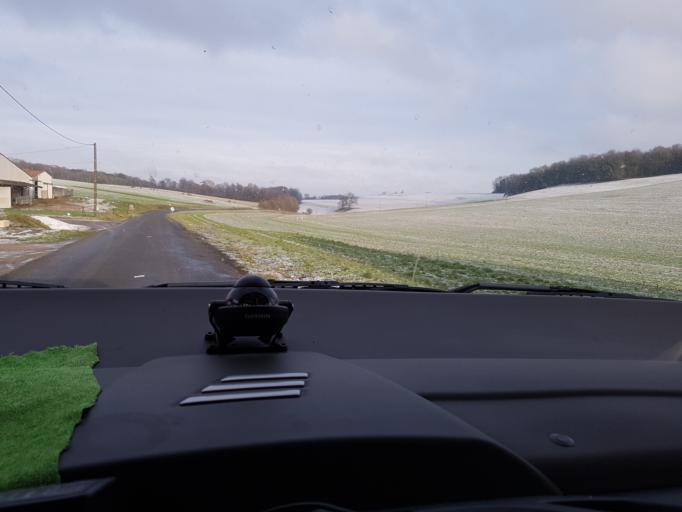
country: FR
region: Champagne-Ardenne
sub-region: Departement des Ardennes
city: Tournes
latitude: 49.7336
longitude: 4.5692
